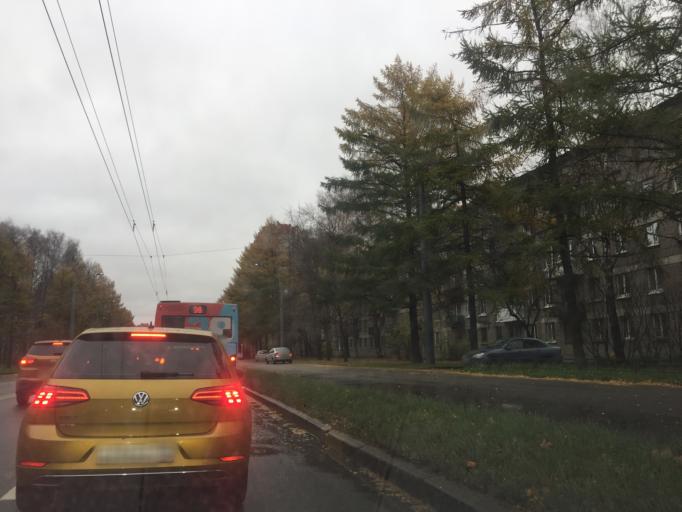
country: RU
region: St.-Petersburg
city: Sosnovka
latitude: 60.0168
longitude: 30.3624
